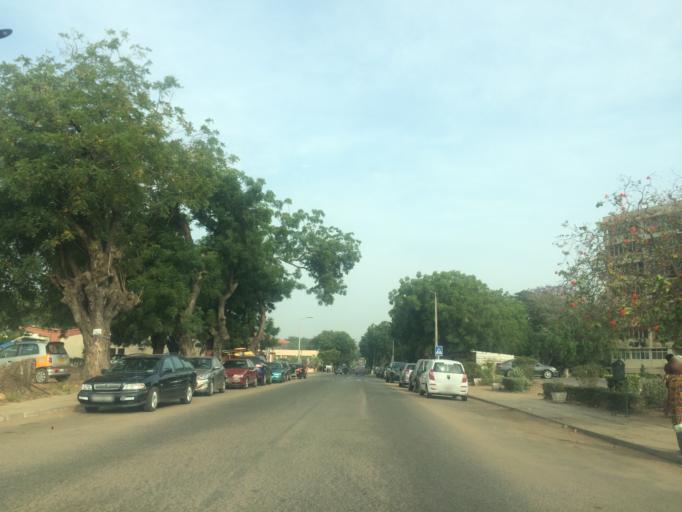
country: GH
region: Greater Accra
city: Accra
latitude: 5.5375
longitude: -0.2274
